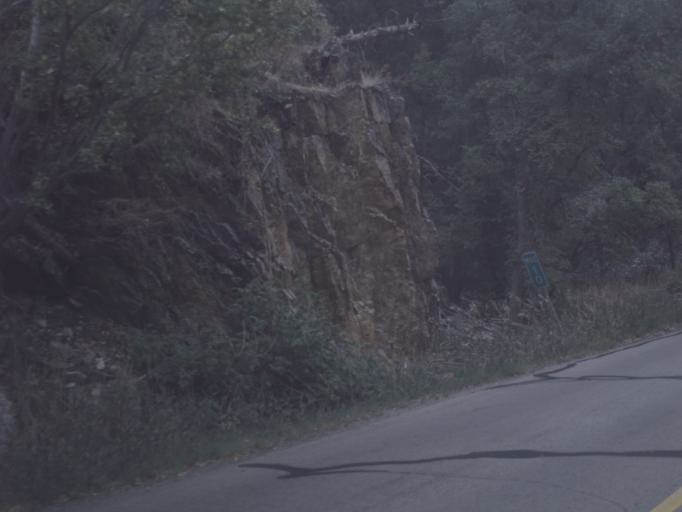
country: US
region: Utah
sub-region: Utah County
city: Cedar Hills
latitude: 40.4433
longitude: -111.7084
